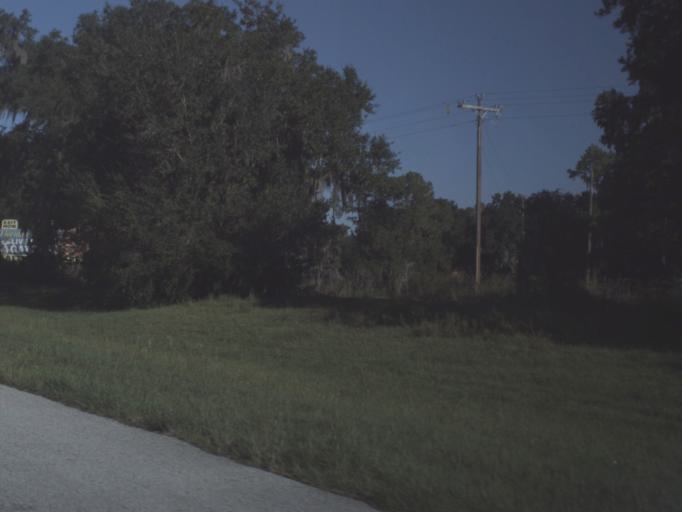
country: US
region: Florida
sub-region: Sumter County
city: Wildwood
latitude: 28.8279
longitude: -82.0292
